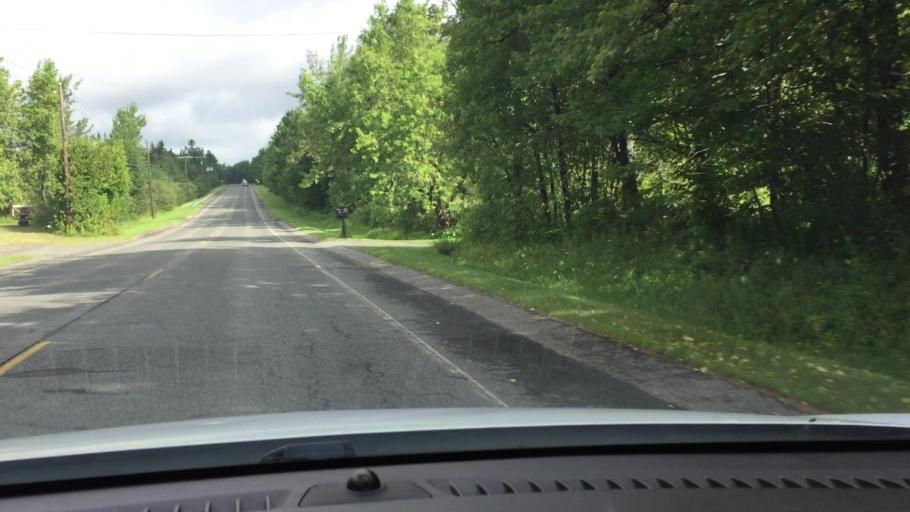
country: US
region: Massachusetts
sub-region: Berkshire County
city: Hinsdale
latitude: 42.4412
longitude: -73.0505
